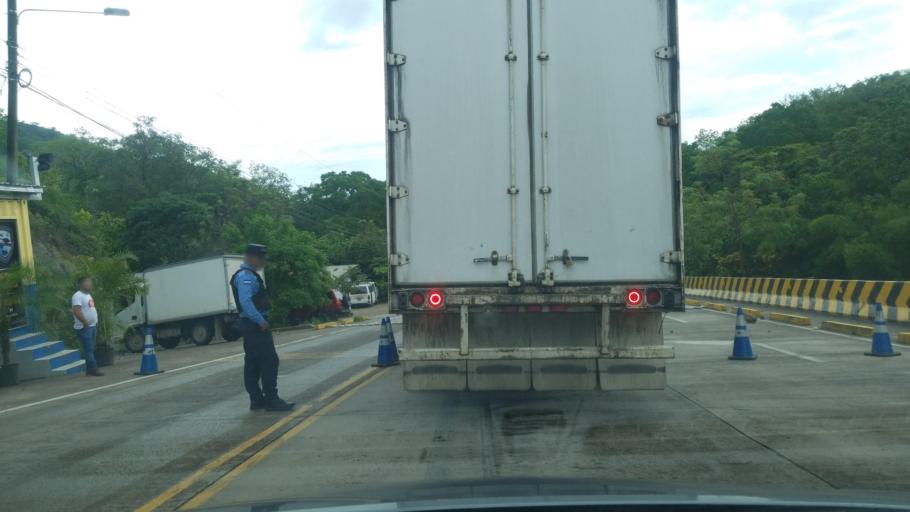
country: HN
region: Copan
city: Copan
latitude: 14.8572
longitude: -89.2229
